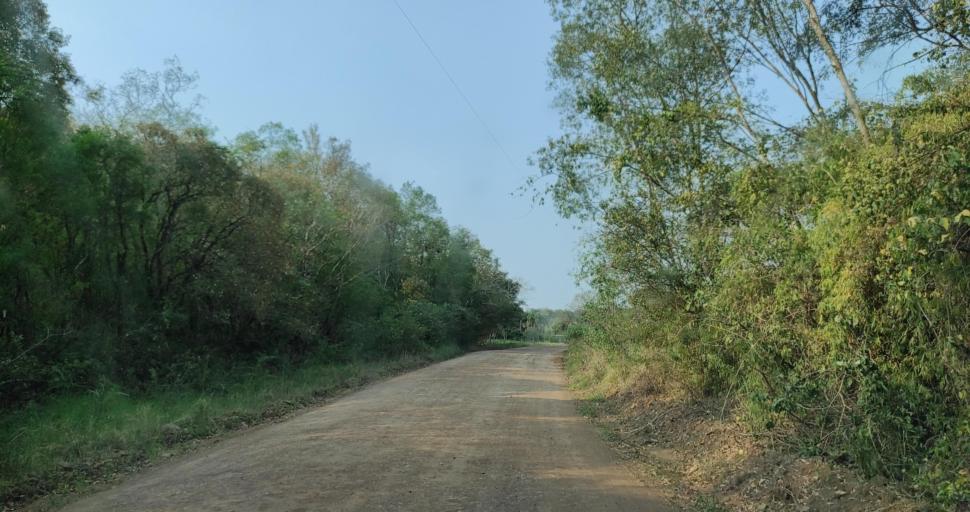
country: AR
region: Misiones
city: Cerro Azul
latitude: -27.6262
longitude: -55.5291
